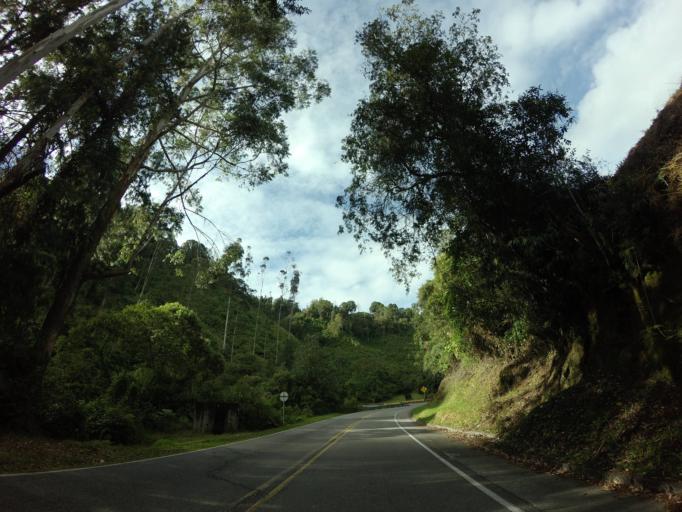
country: CO
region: Tolima
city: Herveo
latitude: 5.1372
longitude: -75.1802
